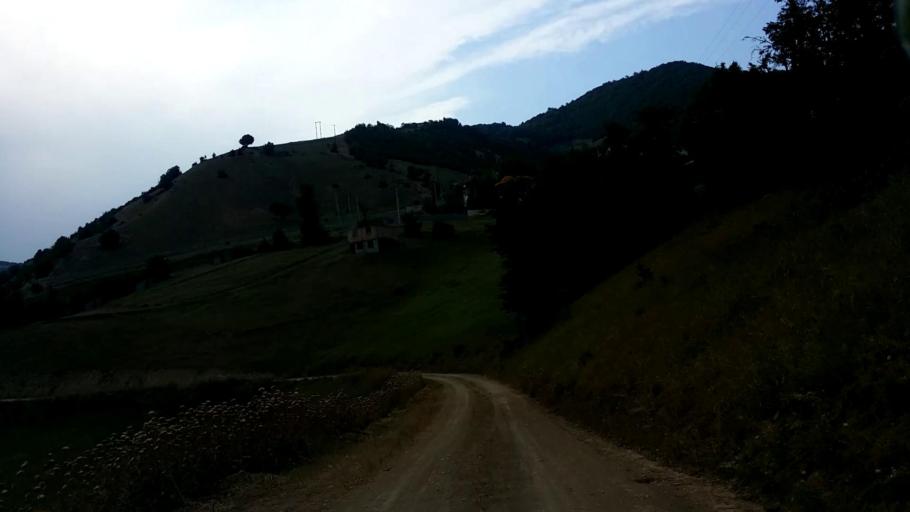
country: IR
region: Mazandaran
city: Chalus
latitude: 36.5524
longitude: 51.2914
